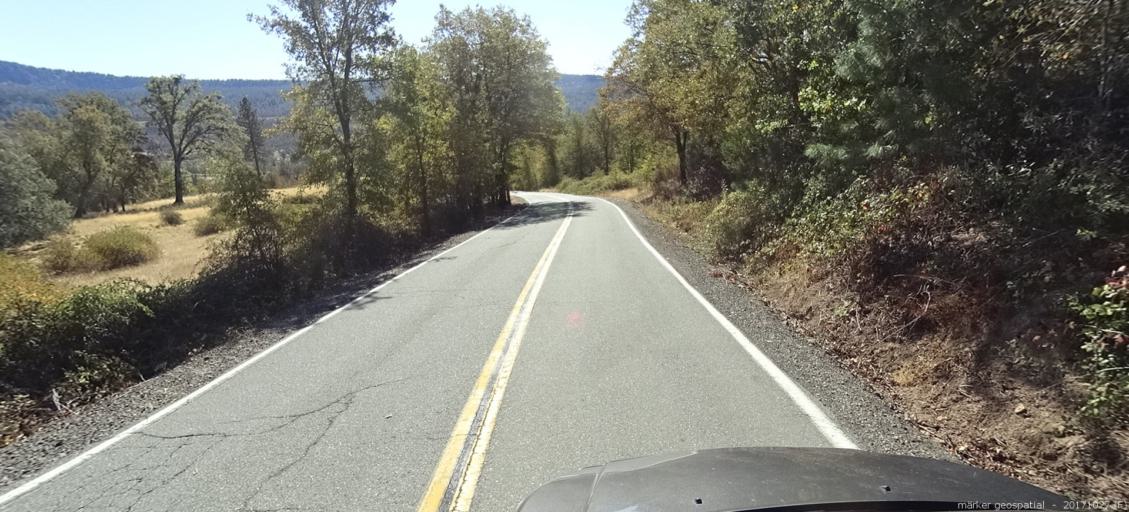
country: US
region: California
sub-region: Shasta County
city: Bella Vista
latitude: 40.7508
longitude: -121.9952
